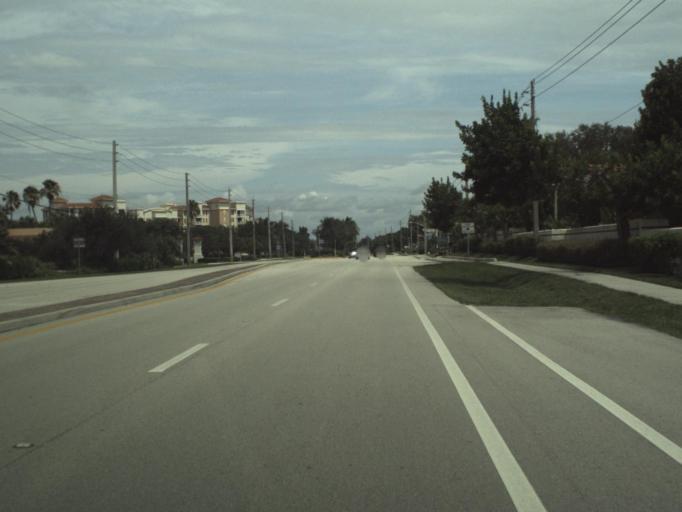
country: US
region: Florida
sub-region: Palm Beach County
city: Jupiter
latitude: 26.9245
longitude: -80.0758
